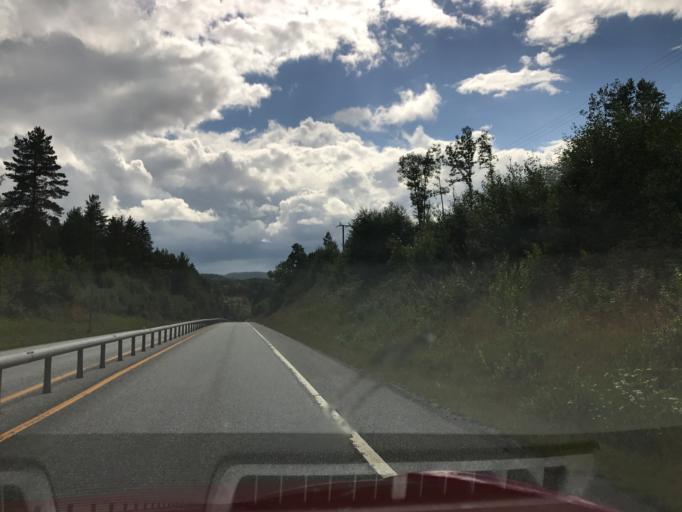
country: NO
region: Aust-Agder
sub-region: Gjerstad
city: Gjerstad
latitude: 58.8495
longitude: 9.1165
